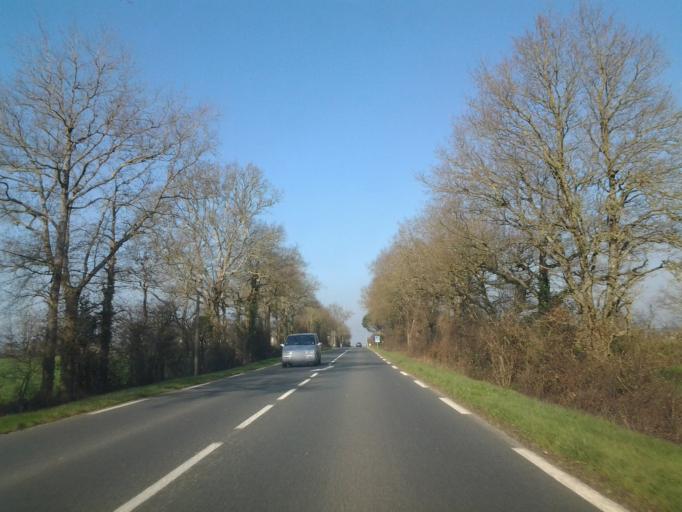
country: FR
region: Pays de la Loire
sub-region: Departement de la Vendee
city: Mache
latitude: 46.7849
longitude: -1.6954
